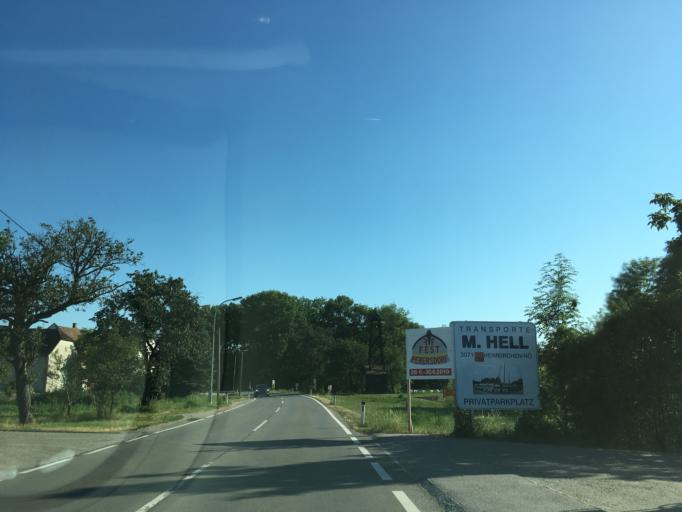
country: AT
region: Lower Austria
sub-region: Politischer Bezirk Sankt Polten
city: Boheimkirchen
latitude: 48.1835
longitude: 15.7599
